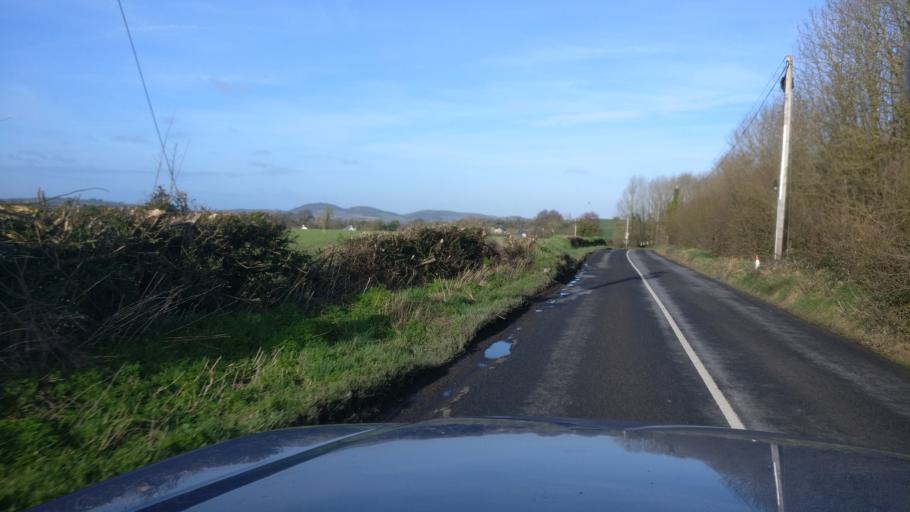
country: IE
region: Leinster
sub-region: Laois
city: Stradbally
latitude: 52.9539
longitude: -7.1988
